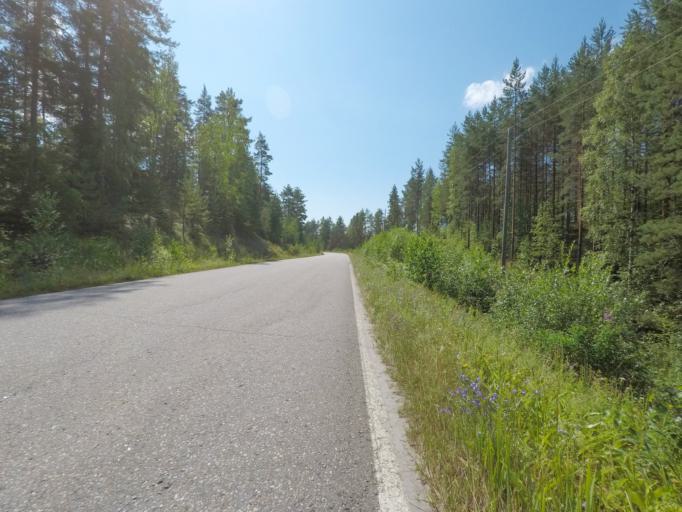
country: FI
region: Southern Savonia
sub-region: Mikkeli
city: Puumala
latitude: 61.5044
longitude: 28.1673
